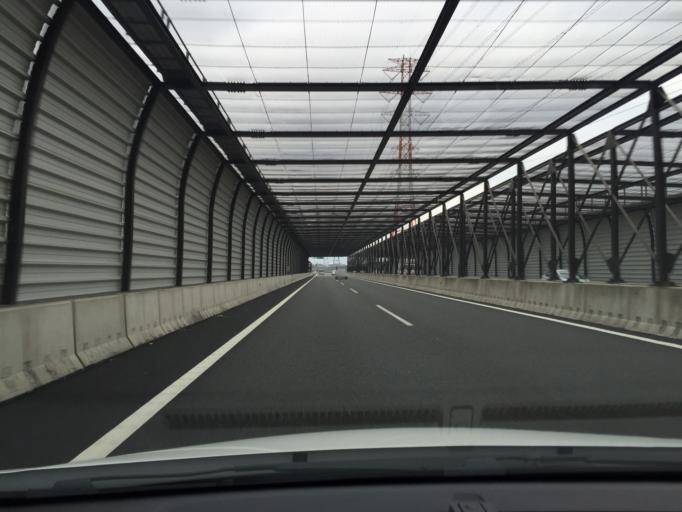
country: JP
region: Saitama
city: Sakado
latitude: 35.9753
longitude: 139.4547
